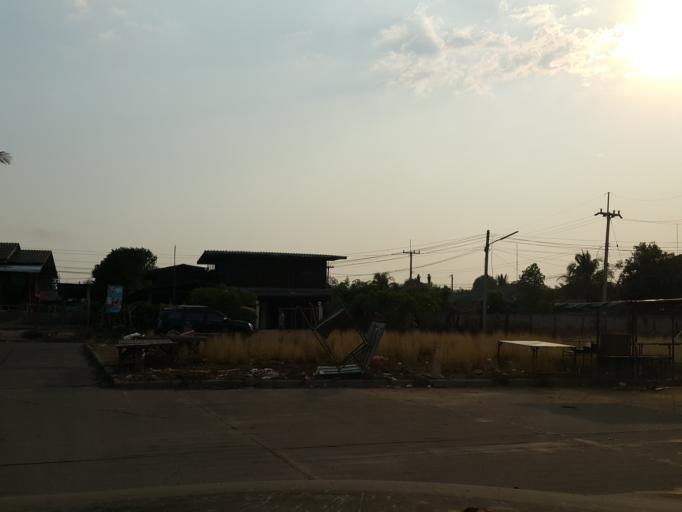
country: TH
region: Lamphun
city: Li
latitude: 17.8006
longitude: 98.9476
